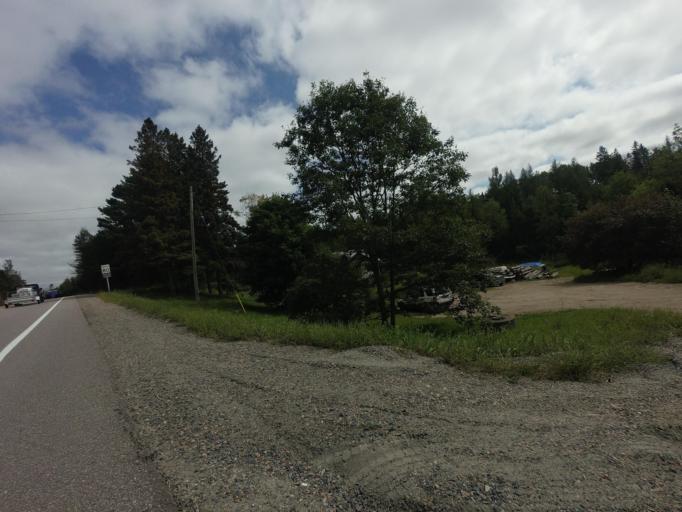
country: CA
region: Ontario
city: Bancroft
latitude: 44.9075
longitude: -78.3729
